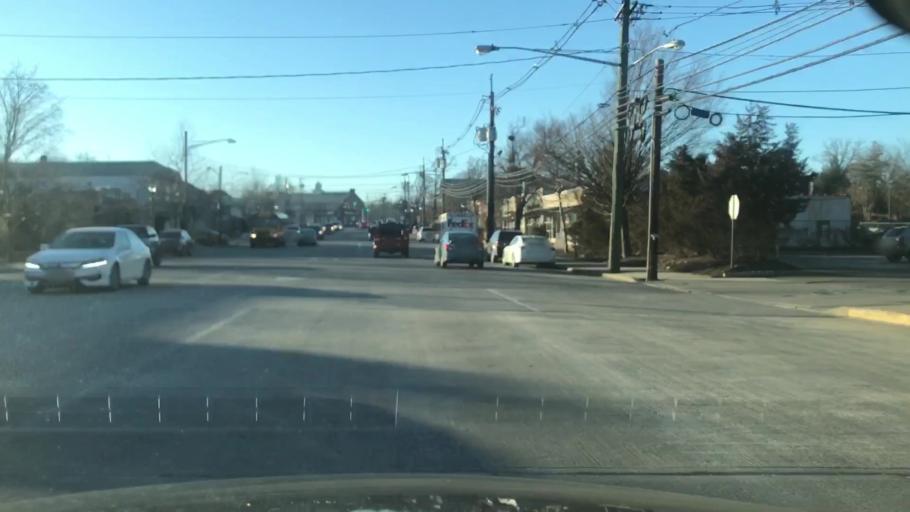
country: US
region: New Jersey
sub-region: Essex County
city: Northfield
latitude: 40.7737
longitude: -74.3216
